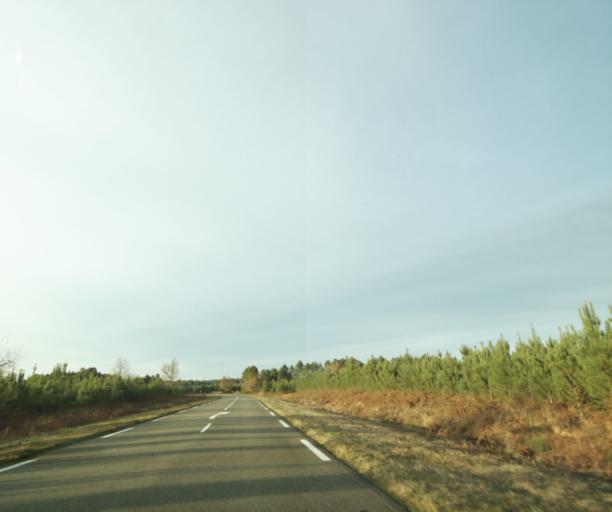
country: FR
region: Aquitaine
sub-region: Departement des Landes
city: Gabarret
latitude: 44.0841
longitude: -0.0739
